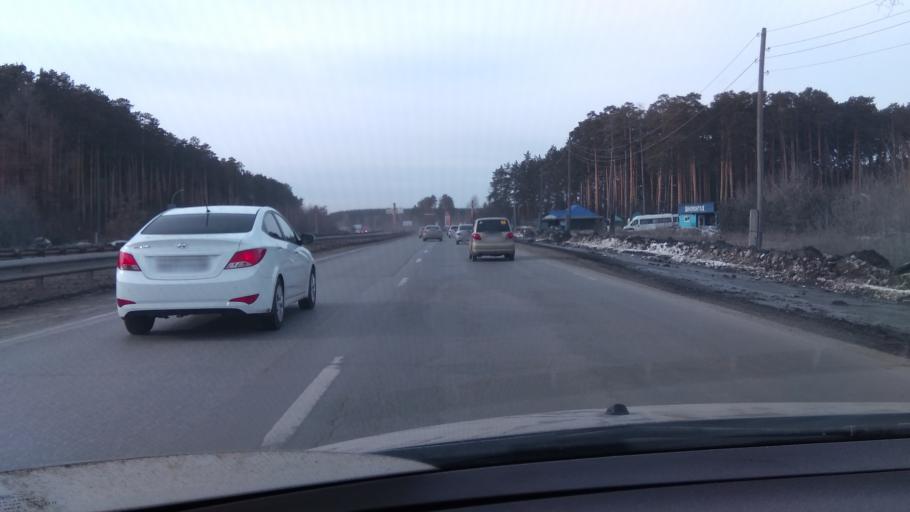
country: RU
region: Sverdlovsk
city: Shirokaya Rechka
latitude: 56.8162
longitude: 60.5118
